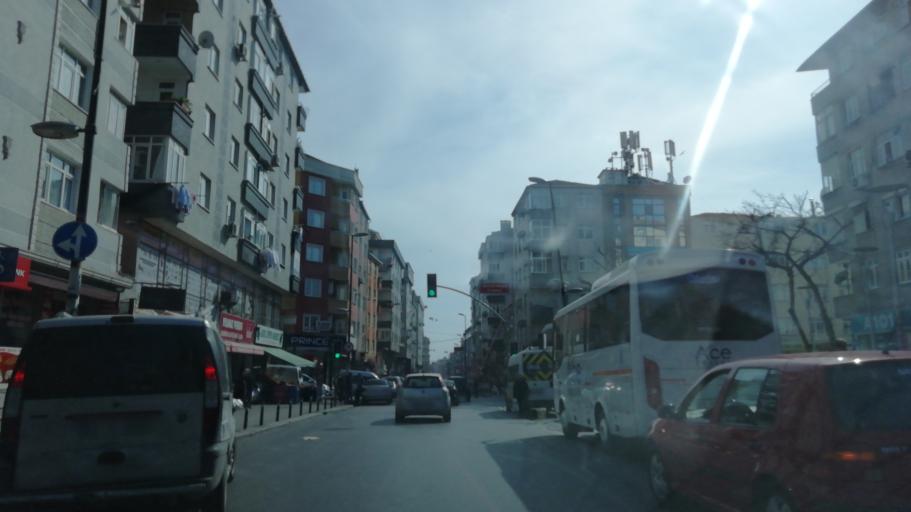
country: TR
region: Istanbul
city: Bahcelievler
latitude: 41.0012
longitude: 28.8387
